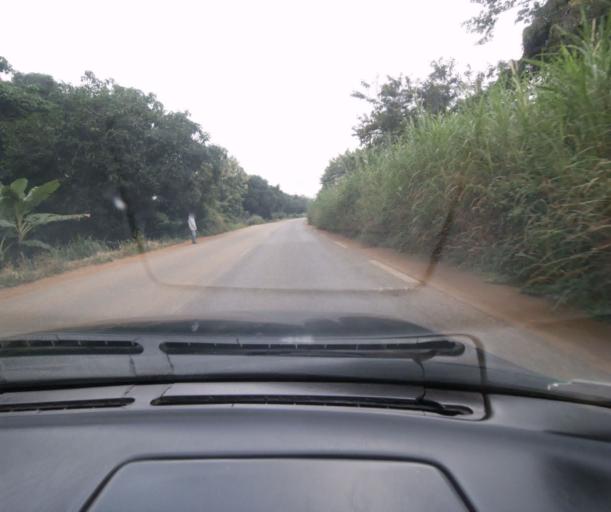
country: CM
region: Centre
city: Ombesa
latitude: 4.4094
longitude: 11.2479
